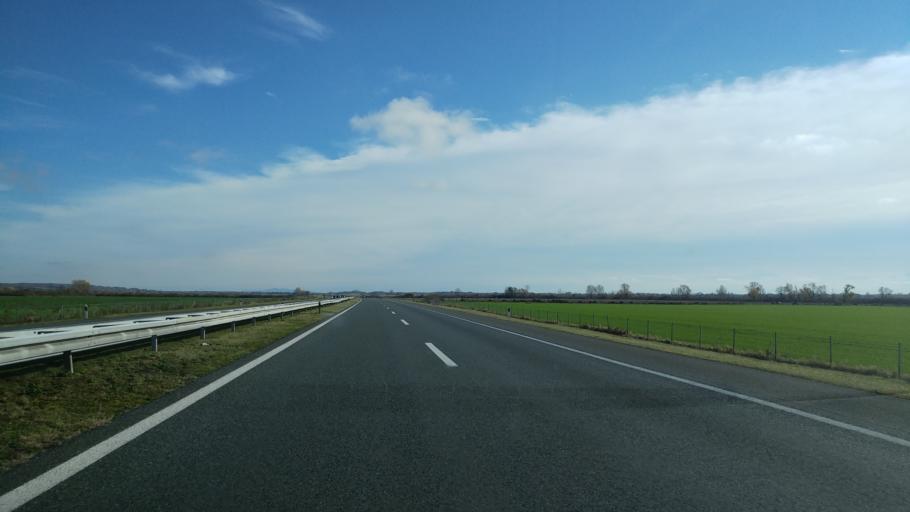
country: HR
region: Brodsko-Posavska
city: Okucani
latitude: 45.2734
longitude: 17.1320
